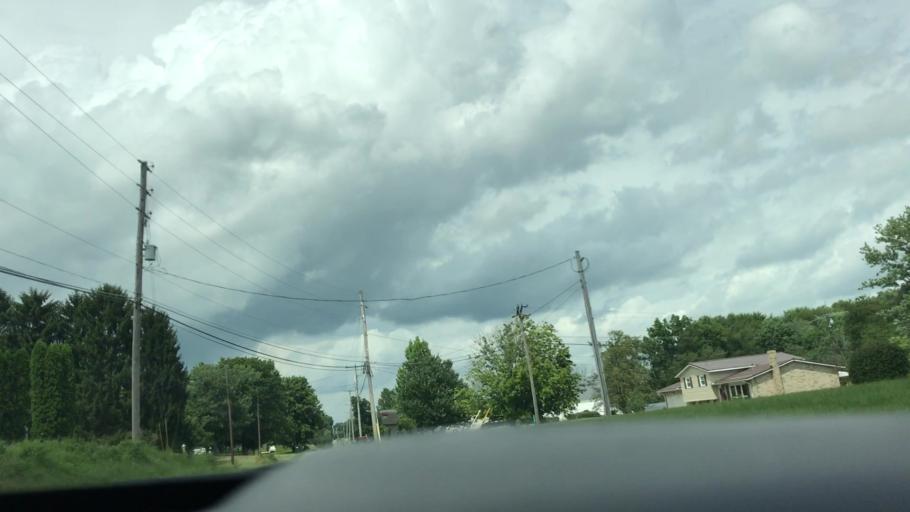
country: US
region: Ohio
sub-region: Stark County
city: Massillon
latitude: 40.7764
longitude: -81.5646
